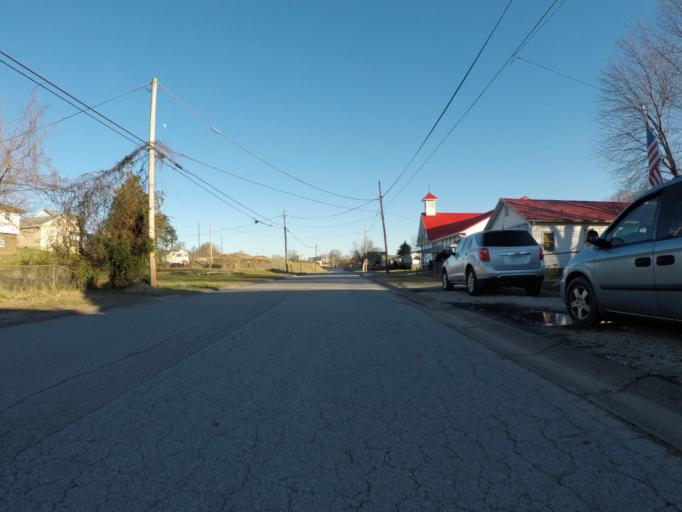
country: US
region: West Virginia
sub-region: Wayne County
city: Kenova
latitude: 38.3994
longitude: -82.5852
